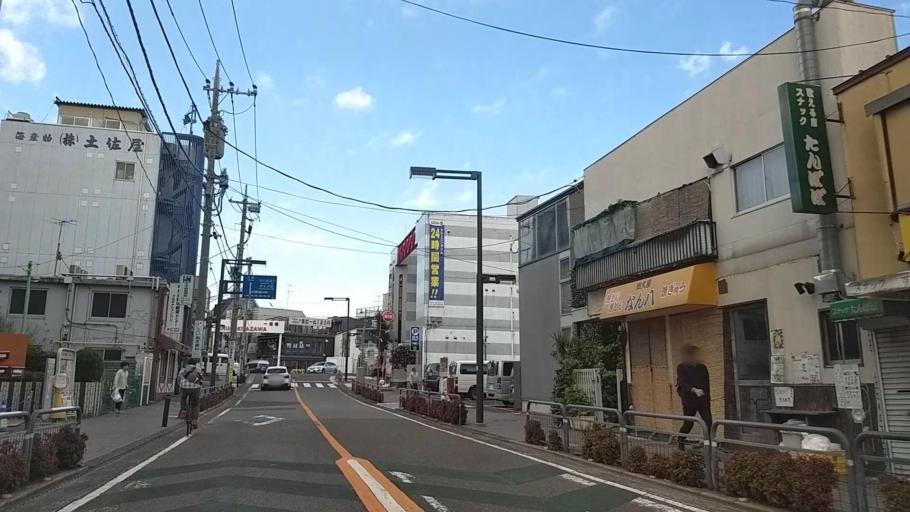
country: JP
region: Tokyo
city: Tokyo
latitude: 35.6625
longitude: 139.6701
